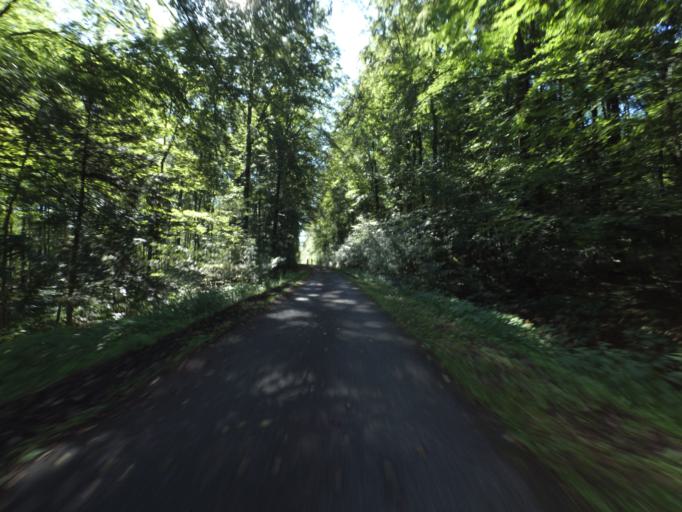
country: DE
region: Rheinland-Pfalz
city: Dierfeld
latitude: 50.0752
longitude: 6.8785
